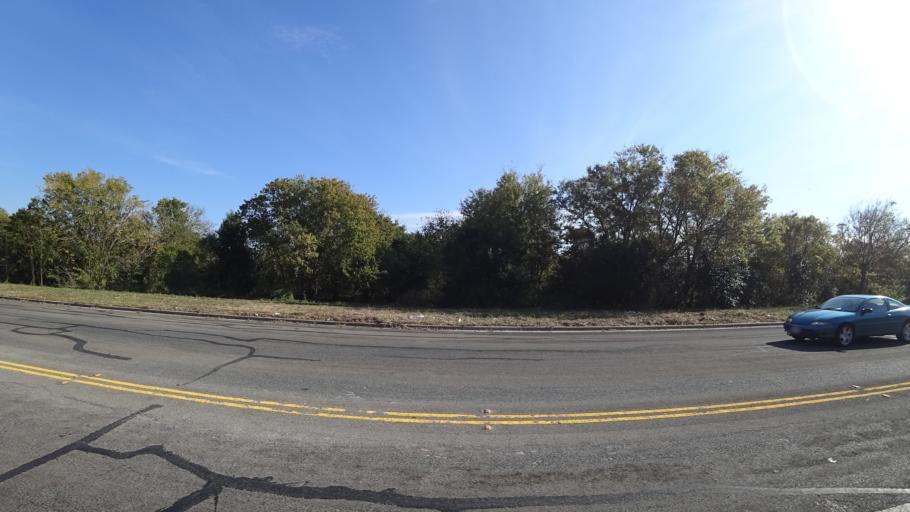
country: US
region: Texas
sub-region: Travis County
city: Pflugerville
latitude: 30.4056
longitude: -97.6435
